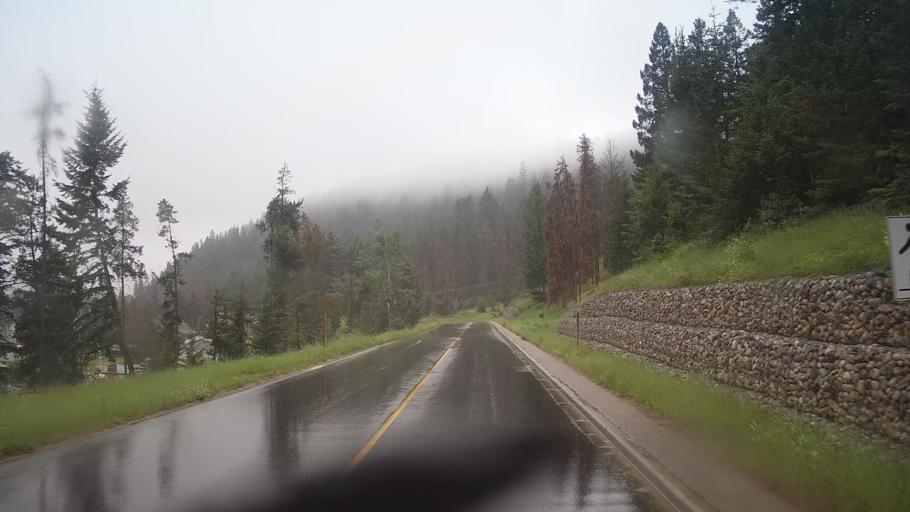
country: CA
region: Alberta
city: Jasper Park Lodge
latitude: 52.8854
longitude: -118.0841
